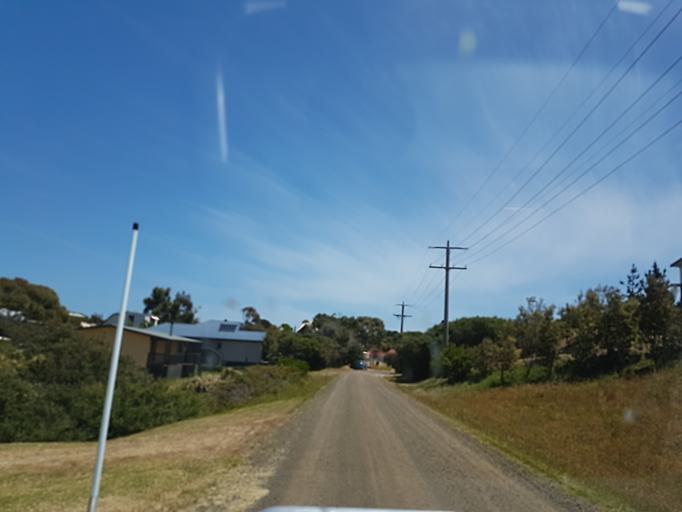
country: AU
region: Victoria
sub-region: Bass Coast
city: North Wonthaggi
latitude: -38.7000
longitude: 145.8244
